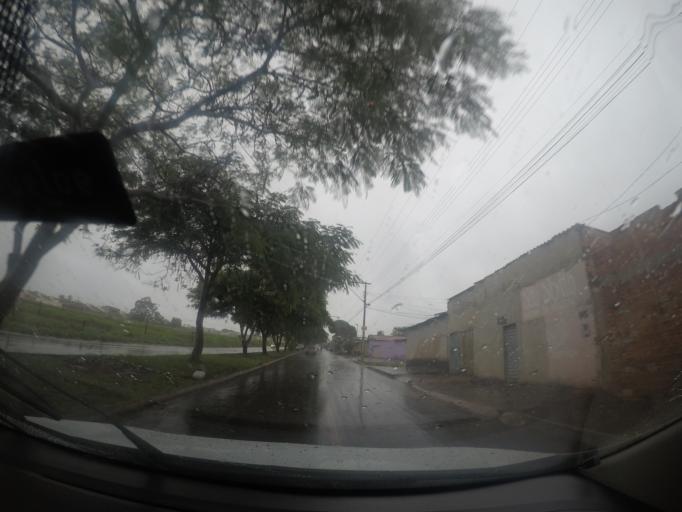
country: BR
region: Goias
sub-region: Goiania
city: Goiania
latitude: -16.5965
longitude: -49.3258
